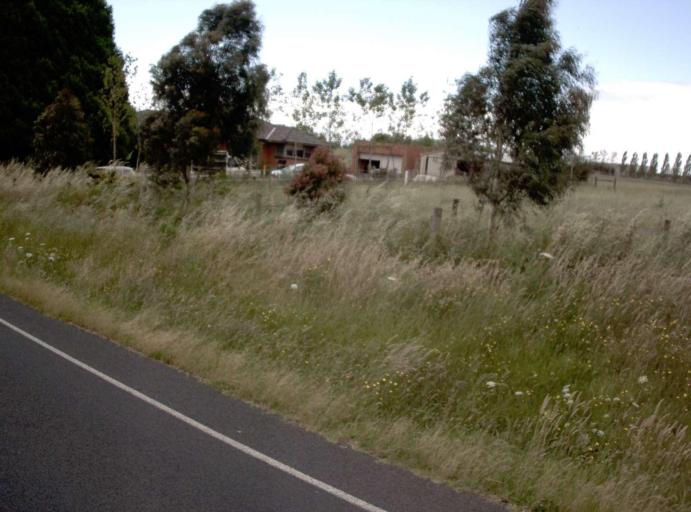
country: AU
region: Victoria
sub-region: Baw Baw
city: Warragul
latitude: -38.0934
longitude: 145.9206
